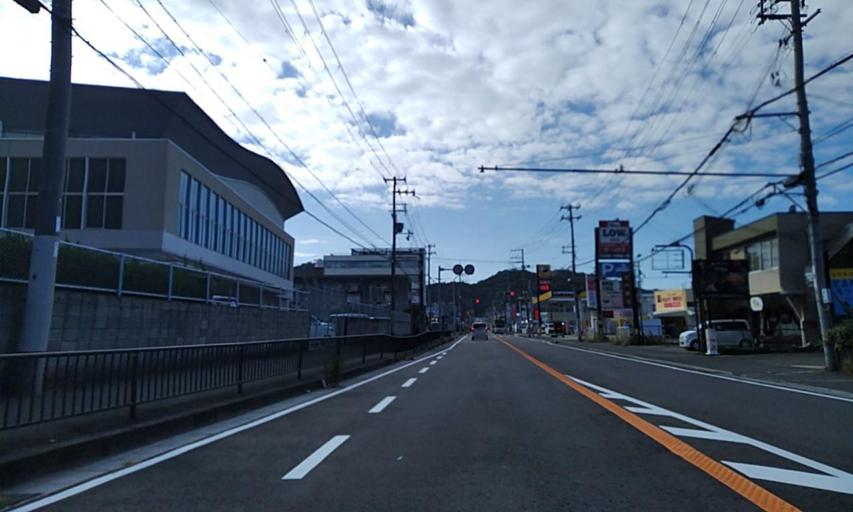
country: JP
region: Wakayama
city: Minato
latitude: 34.2012
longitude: 135.1592
